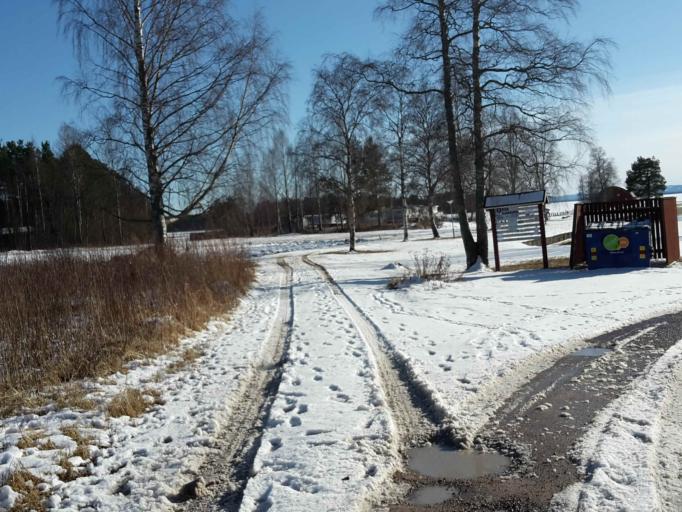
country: SE
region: Dalarna
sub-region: Orsa Kommun
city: Orsa
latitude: 61.1186
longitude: 14.6079
